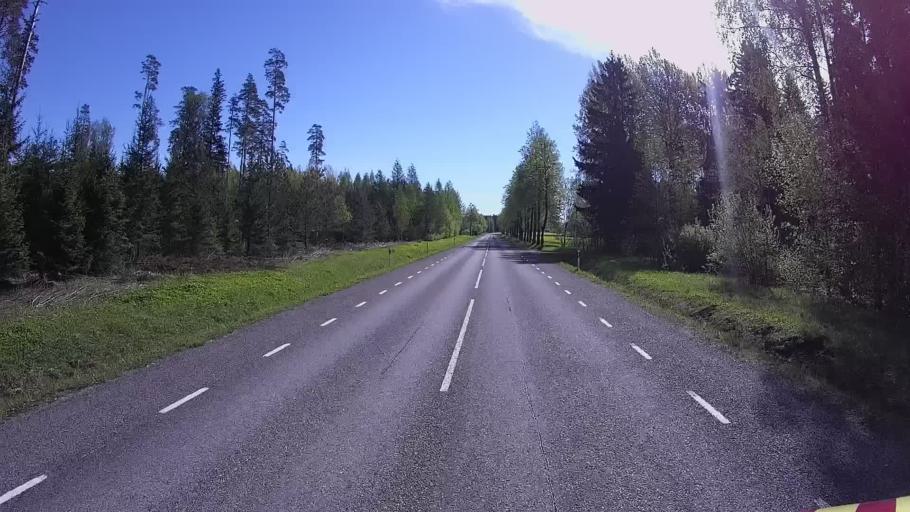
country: EE
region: Polvamaa
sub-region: Raepina vald
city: Rapina
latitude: 58.0969
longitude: 27.4019
